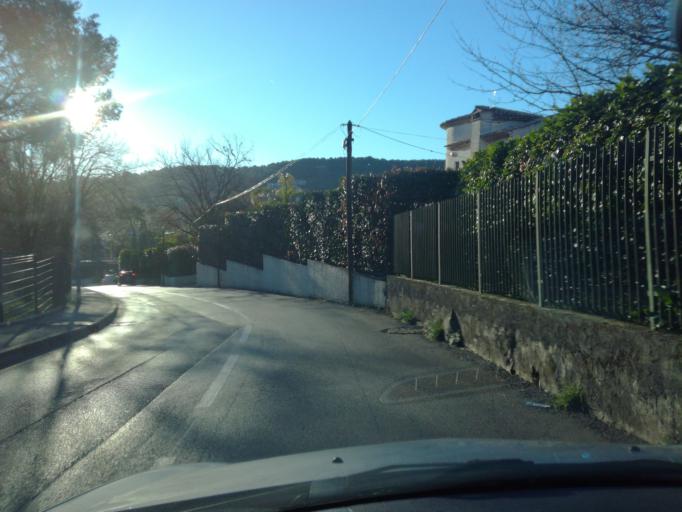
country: FR
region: Provence-Alpes-Cote d'Azur
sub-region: Departement des Alpes-Maritimes
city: La Roquette-sur-Siagne
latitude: 43.6073
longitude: 6.9695
